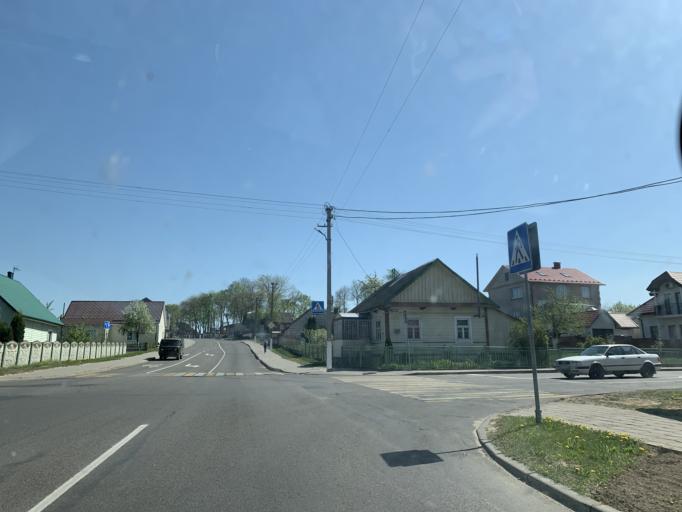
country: BY
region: Minsk
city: Nyasvizh
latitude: 53.2164
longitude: 26.6890
